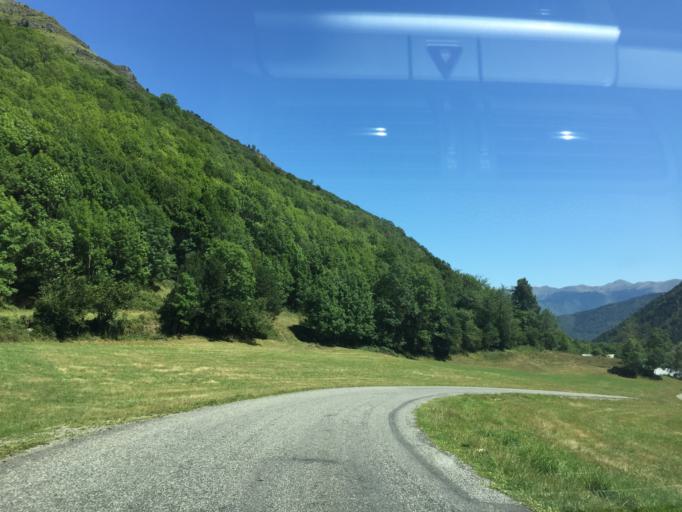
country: FR
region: Midi-Pyrenees
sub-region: Departement des Hautes-Pyrenees
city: Saint-Lary-Soulan
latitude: 42.8508
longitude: 0.3047
